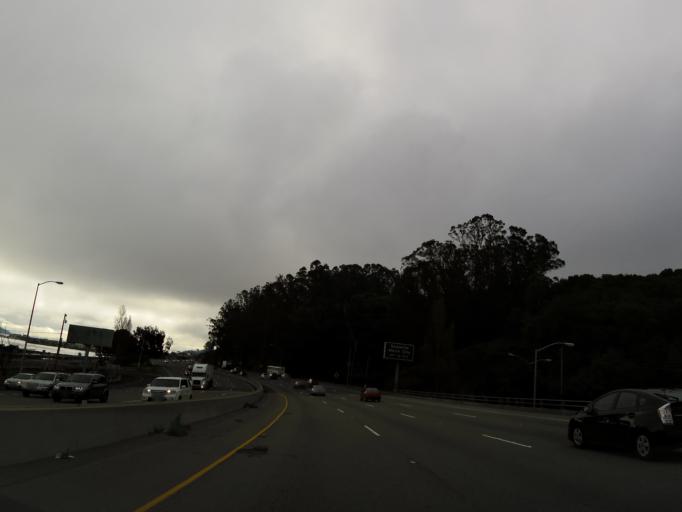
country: US
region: California
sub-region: Marin County
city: Marin City
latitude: 37.8794
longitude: -122.5159
